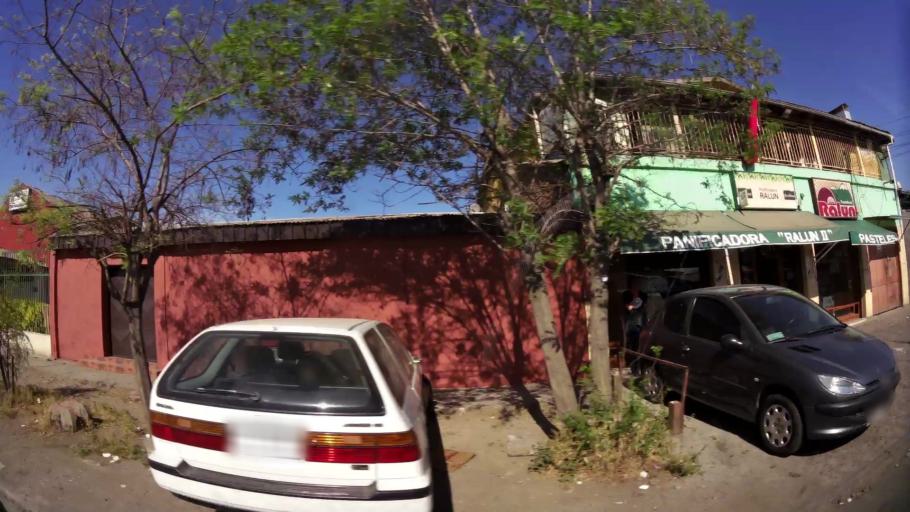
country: CL
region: Santiago Metropolitan
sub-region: Provincia de Santiago
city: Santiago
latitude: -33.5170
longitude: -70.6879
